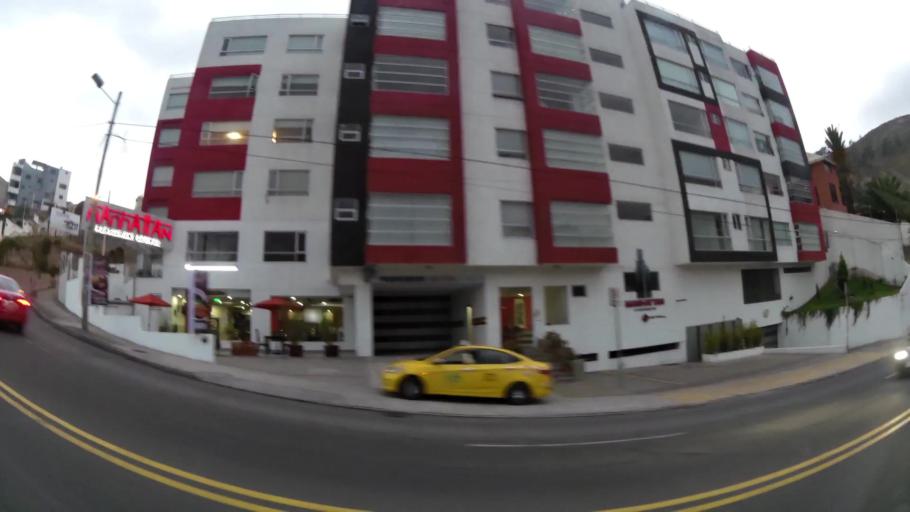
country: EC
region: Tungurahua
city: Ambato
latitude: -1.2553
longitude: -78.6423
